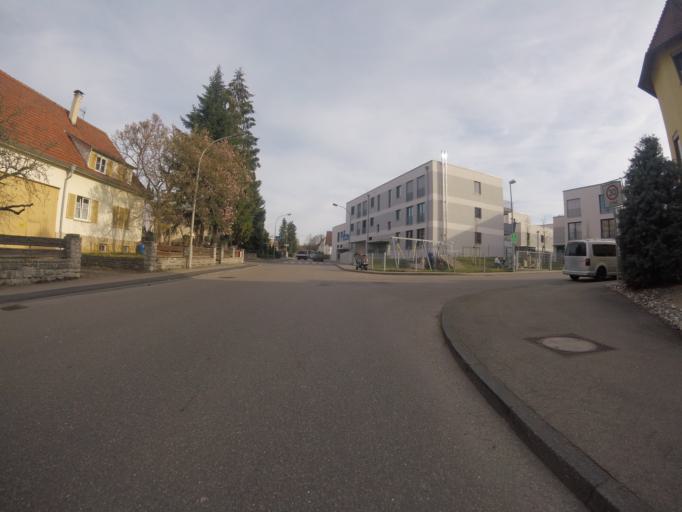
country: DE
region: Baden-Wuerttemberg
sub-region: Regierungsbezirk Stuttgart
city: Grossbottwar
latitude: 48.9972
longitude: 9.2956
